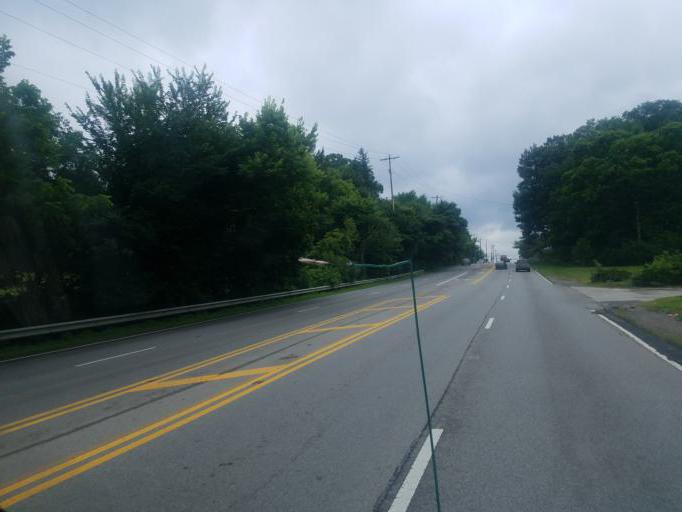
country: US
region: Ohio
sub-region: Franklin County
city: Whitehall
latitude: 39.9768
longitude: -82.8690
